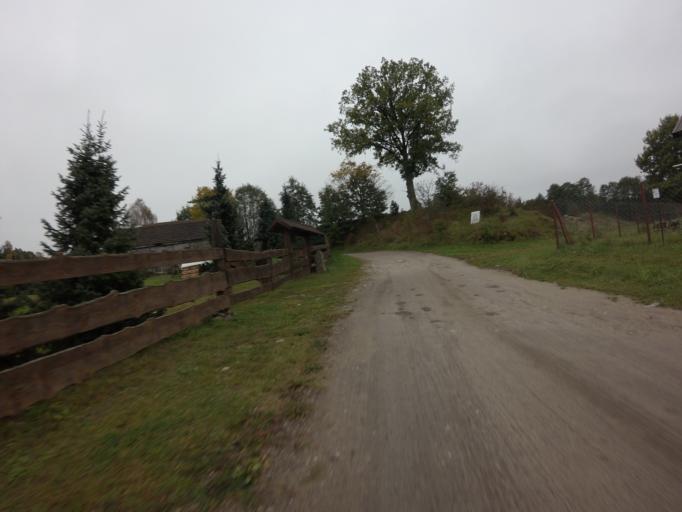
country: PL
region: Pomeranian Voivodeship
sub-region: Powiat kartuski
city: Stezyca
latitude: 54.1727
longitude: 17.9544
